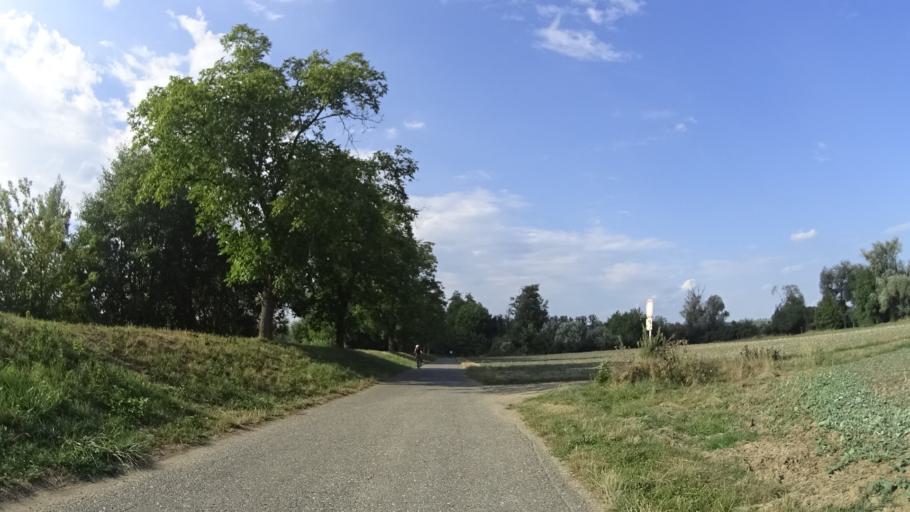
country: CZ
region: Zlin
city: Spytihnev
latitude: 49.1431
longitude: 17.5055
